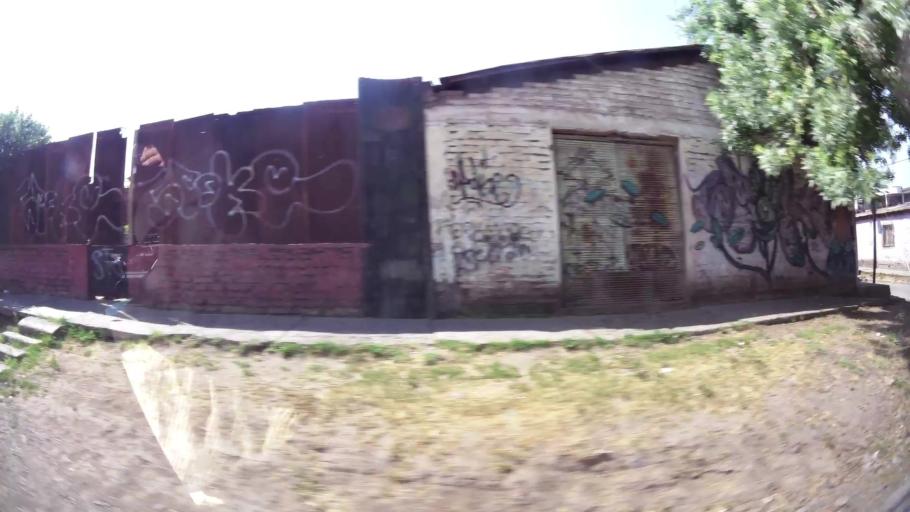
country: CL
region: Santiago Metropolitan
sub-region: Provincia de Santiago
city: Lo Prado
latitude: -33.4326
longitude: -70.7303
